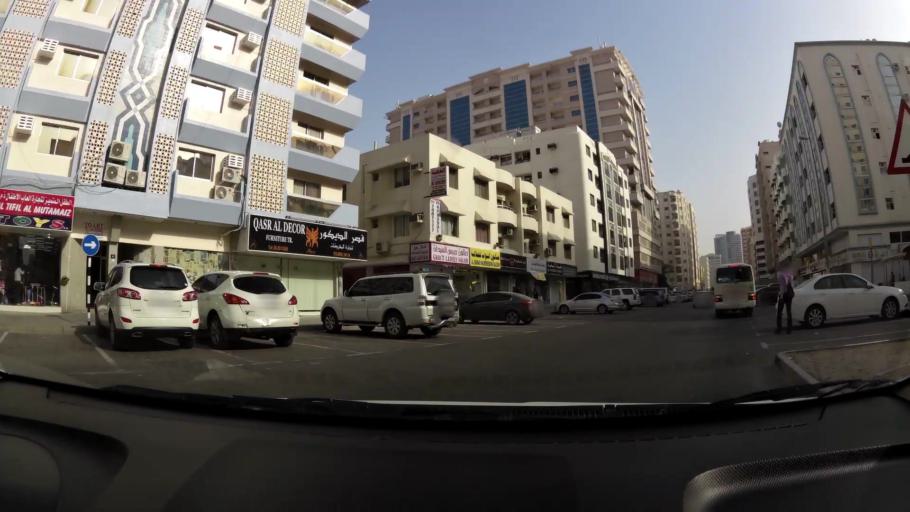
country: AE
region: Ash Shariqah
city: Sharjah
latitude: 25.3355
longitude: 55.3988
